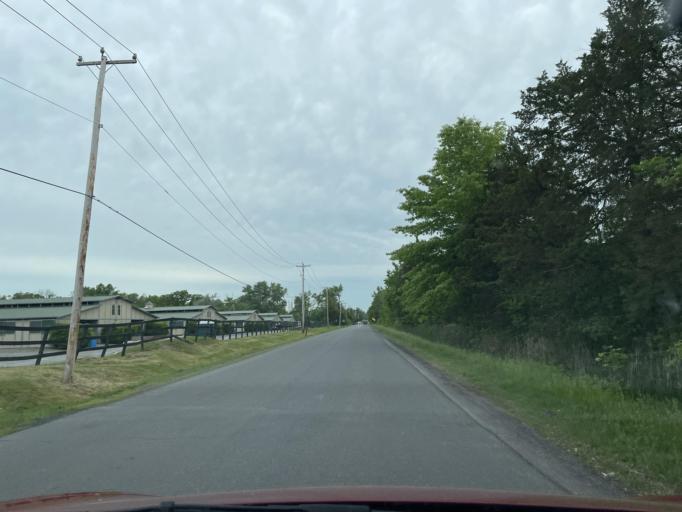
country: US
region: New York
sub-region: Ulster County
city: Saugerties
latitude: 42.0973
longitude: -73.9474
